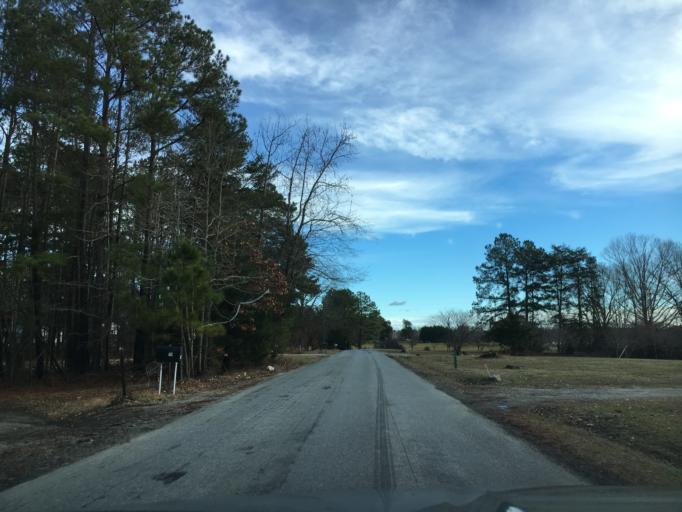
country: US
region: Virginia
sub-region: Nottoway County
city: Crewe
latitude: 37.2367
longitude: -78.2408
